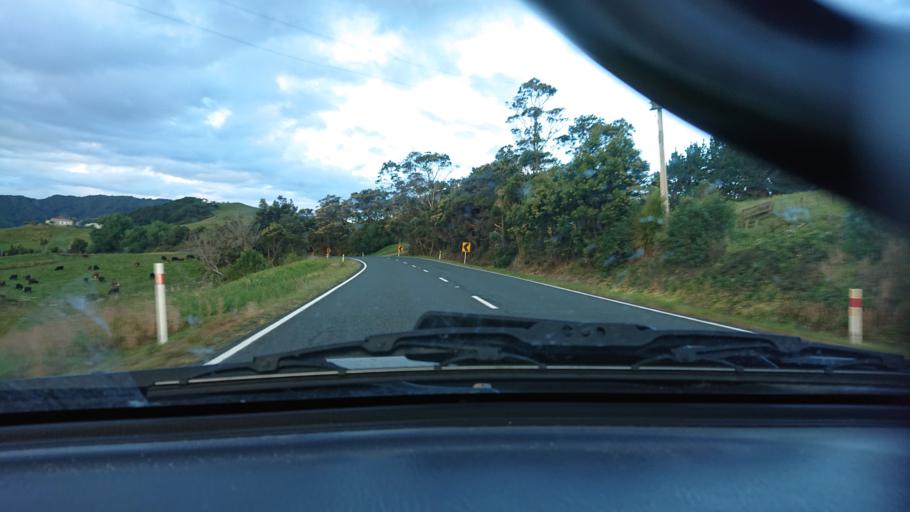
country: NZ
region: Auckland
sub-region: Auckland
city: Parakai
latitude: -36.4736
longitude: 174.4491
